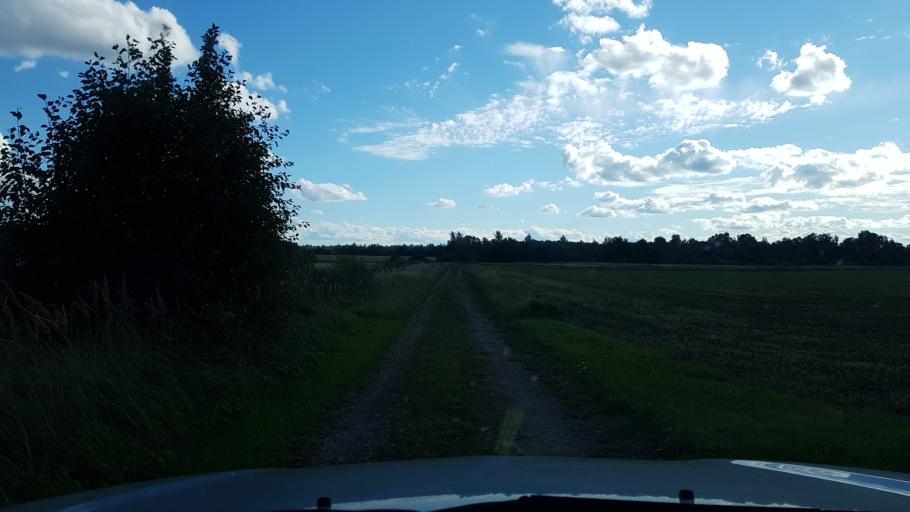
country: EE
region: Harju
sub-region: Rae vald
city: Jueri
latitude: 59.3594
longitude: 24.8557
